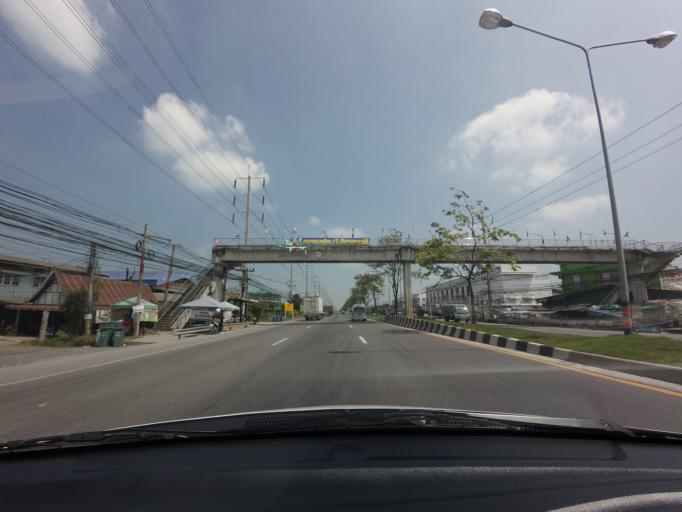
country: TH
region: Chachoengsao
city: Bang Pakong
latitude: 13.5856
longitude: 101.0102
